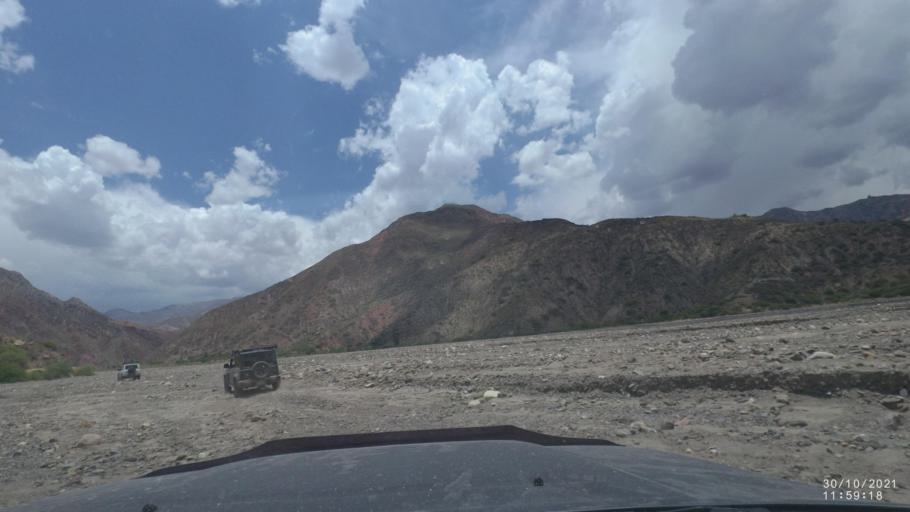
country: BO
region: Cochabamba
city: Colchani
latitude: -17.5252
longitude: -66.6184
